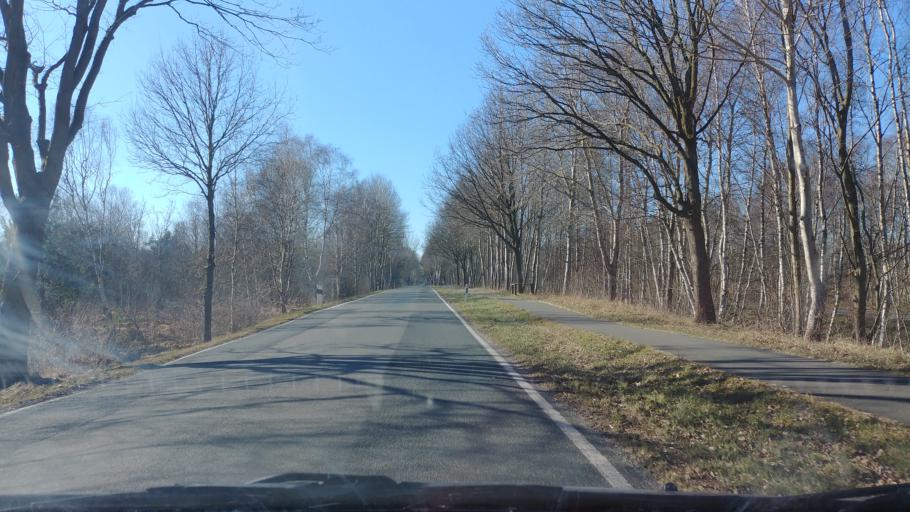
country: DE
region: Lower Saxony
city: Neustadt am Rubenberge
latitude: 52.5053
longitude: 9.4118
